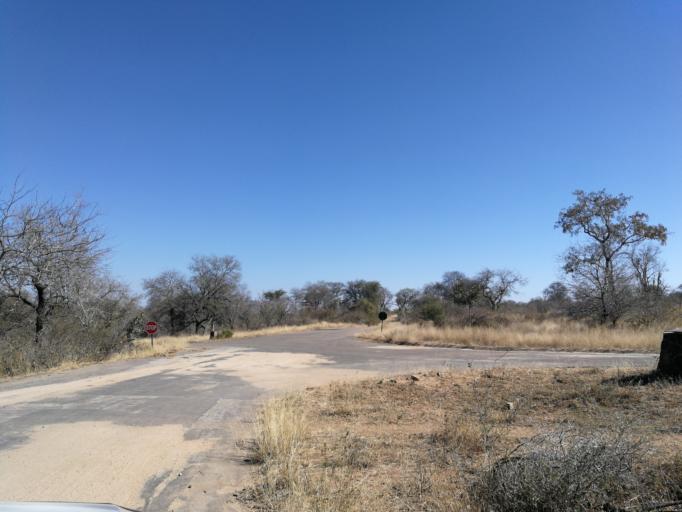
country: ZA
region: Limpopo
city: Thulamahashi
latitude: -24.9832
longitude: 31.5784
